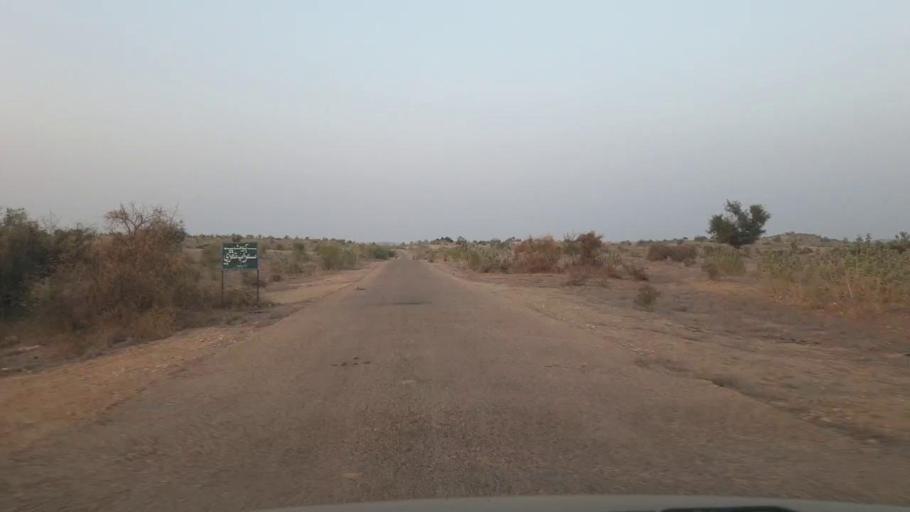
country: PK
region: Sindh
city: Umarkot
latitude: 25.2837
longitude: 70.0773
